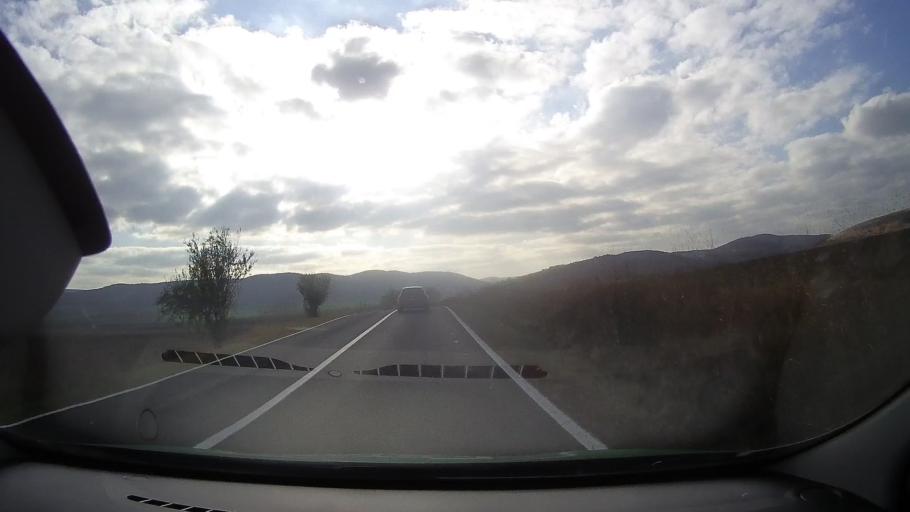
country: RO
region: Tulcea
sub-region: Comuna Nalbant
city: Nicolae Balcescu
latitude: 44.9805
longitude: 28.5492
